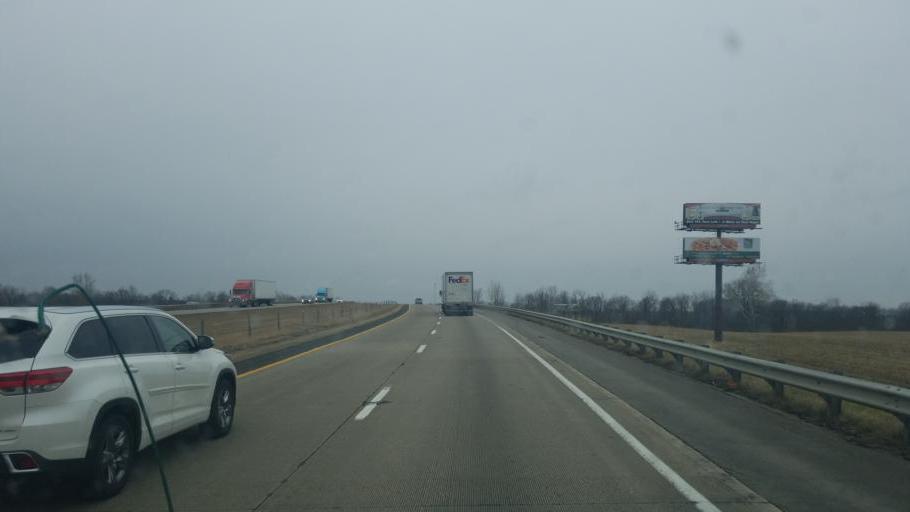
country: US
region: Indiana
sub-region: Henry County
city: Knightstown
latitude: 39.8441
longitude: -85.5448
